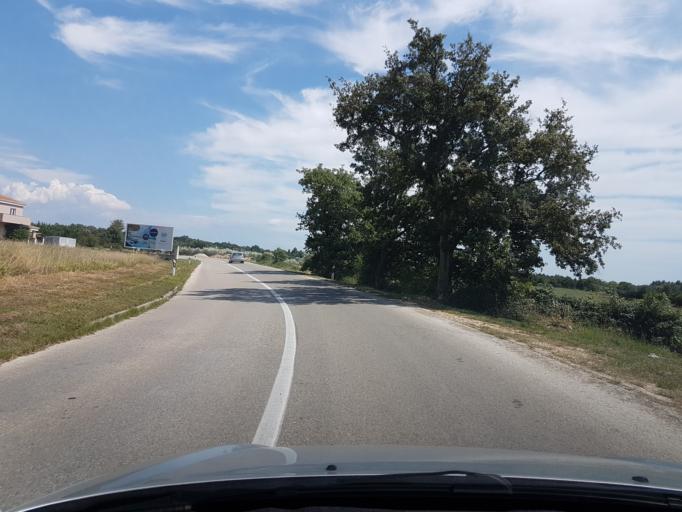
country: HR
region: Istarska
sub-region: Grad Rovinj
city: Rovinj
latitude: 45.1481
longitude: 13.6987
